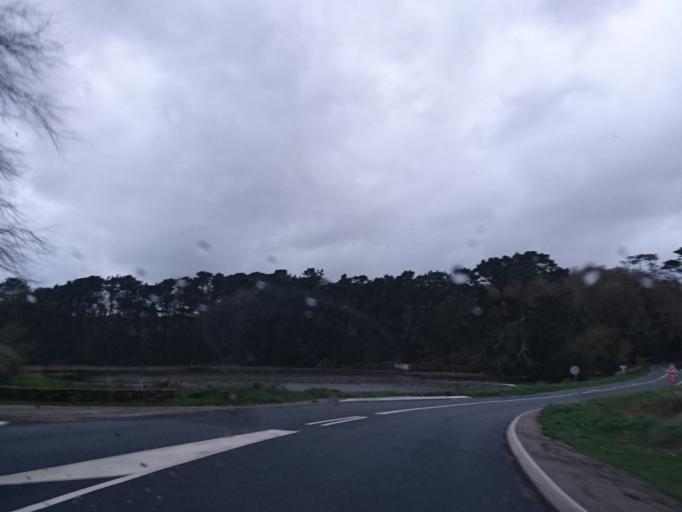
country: FR
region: Brittany
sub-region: Departement du Finistere
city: Le Conquet
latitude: 48.3597
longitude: -4.7509
